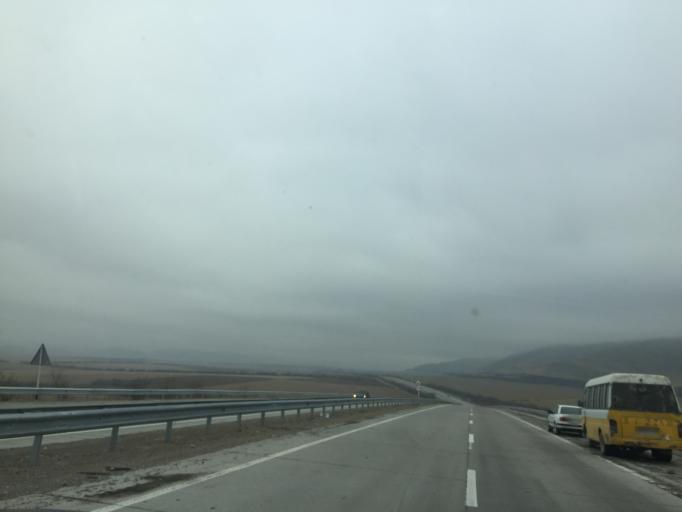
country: KZ
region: Ongtustik Qazaqstan
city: Sastobe
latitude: 42.5413
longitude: 70.0345
